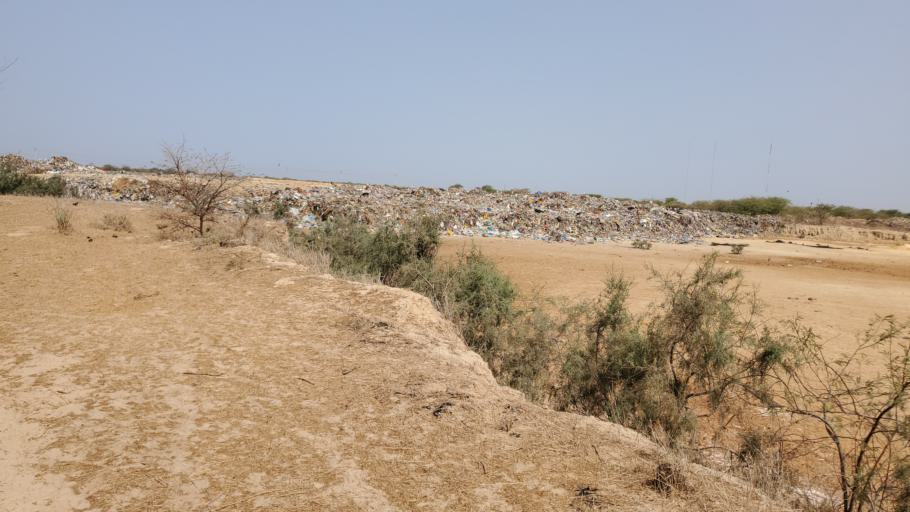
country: SN
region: Saint-Louis
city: Saint-Louis
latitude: 15.9489
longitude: -16.4296
